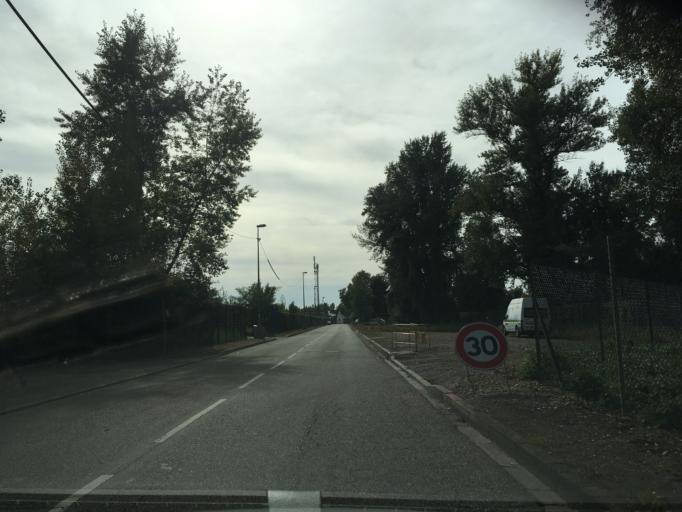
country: DE
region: Baden-Wuerttemberg
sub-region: Freiburg Region
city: Kehl
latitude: 48.5966
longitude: 7.7983
